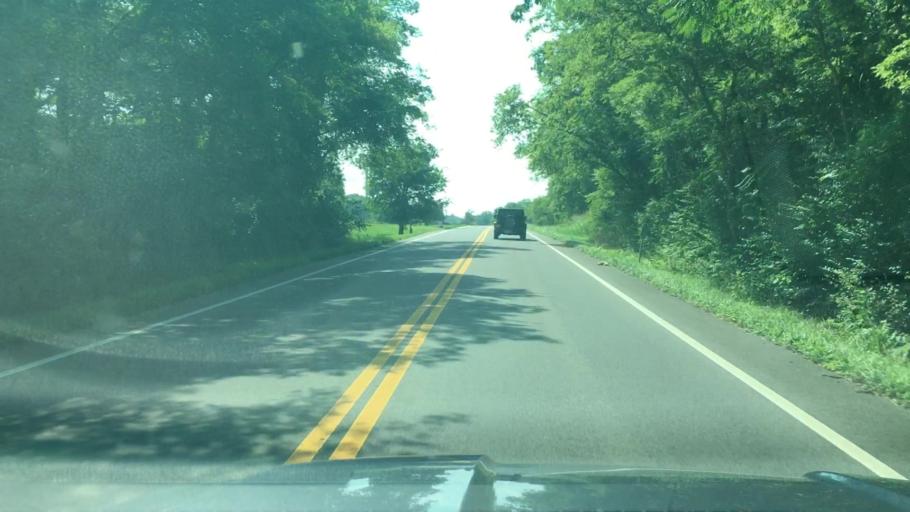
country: US
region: Tennessee
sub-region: Williamson County
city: Nolensville
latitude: 35.8808
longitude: -86.7449
